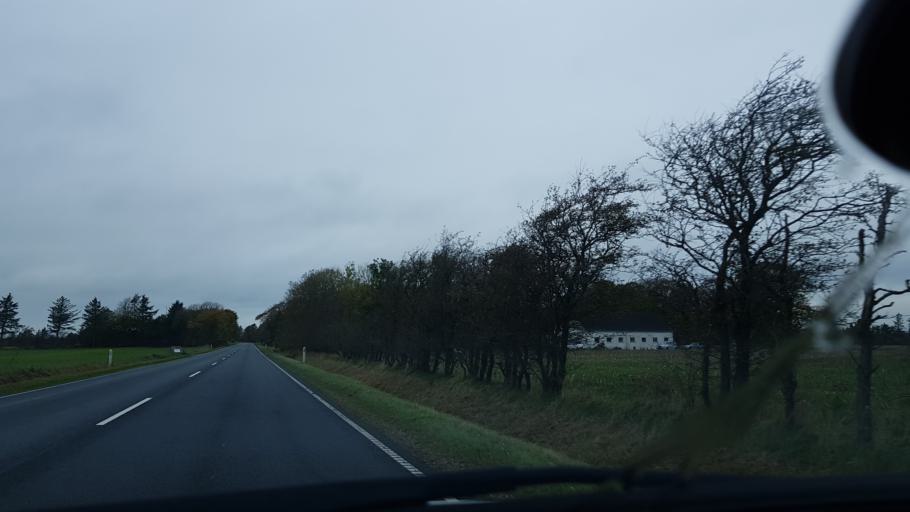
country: DK
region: South Denmark
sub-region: Esbjerg Kommune
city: Ribe
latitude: 55.2899
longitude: 8.8252
